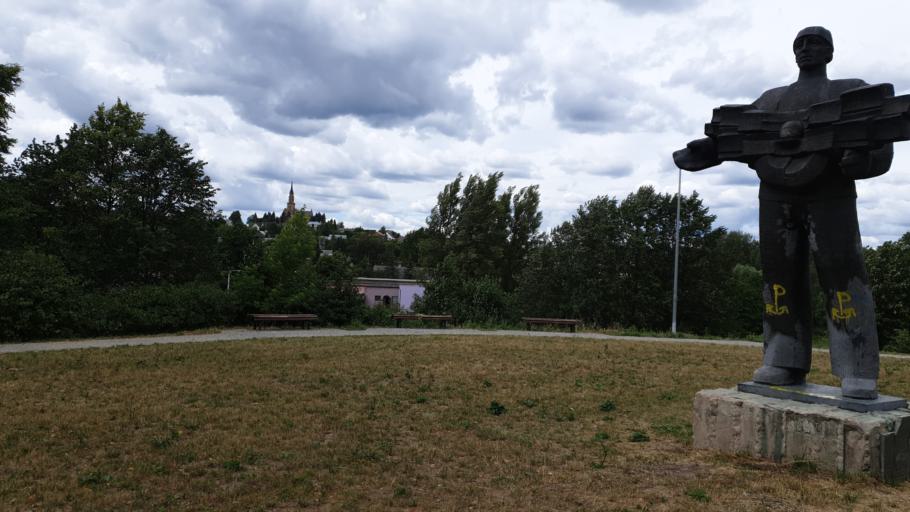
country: LT
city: Skaidiskes
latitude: 54.6912
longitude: 25.4155
